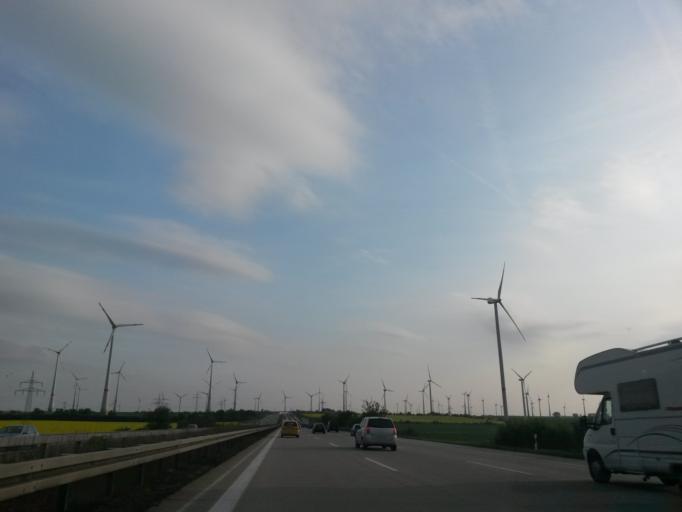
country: DE
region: Saxony-Anhalt
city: Nessa
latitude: 51.1551
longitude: 11.9850
